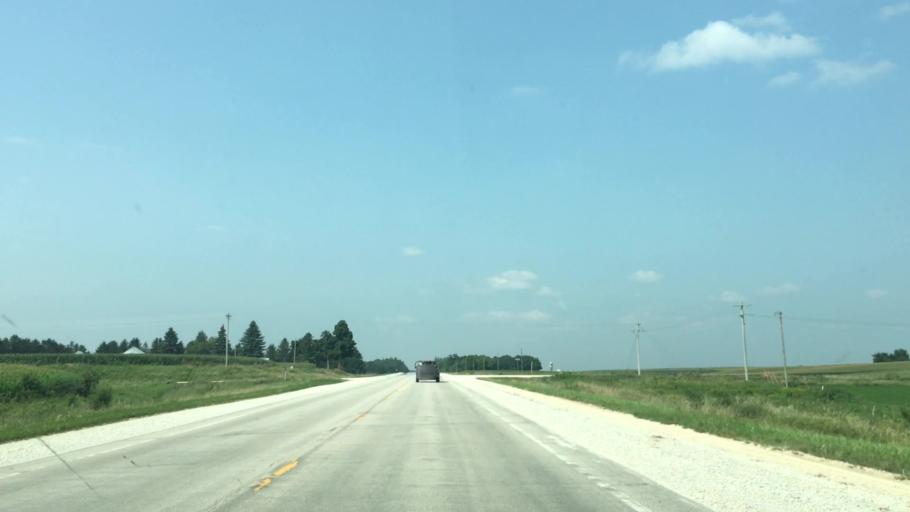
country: US
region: Minnesota
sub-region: Fillmore County
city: Harmony
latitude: 43.4854
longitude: -91.8705
